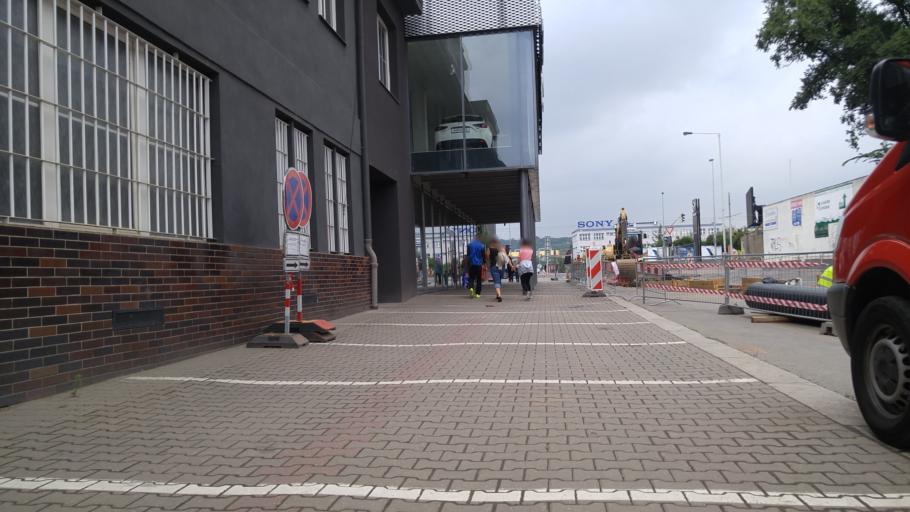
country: CZ
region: Praha
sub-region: Praha 9
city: Vysocany
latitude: 50.1029
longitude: 14.5198
